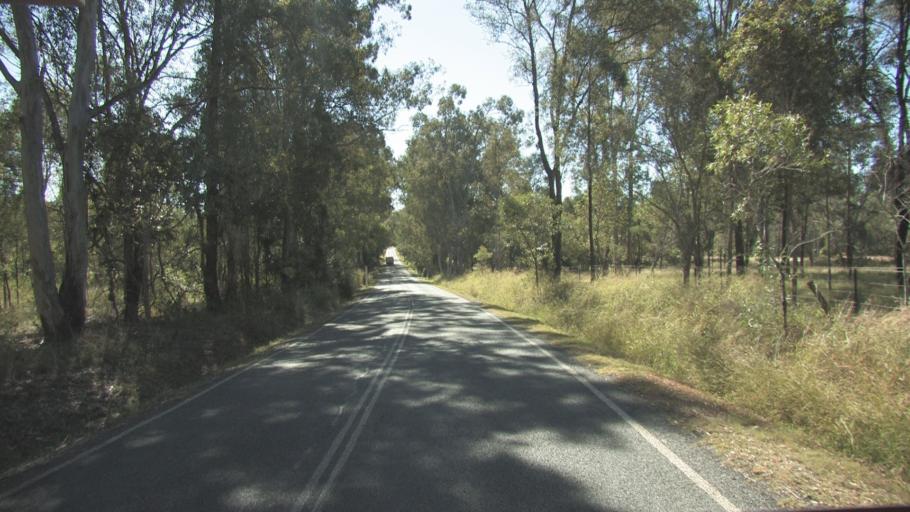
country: AU
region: Queensland
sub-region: Logan
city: Waterford West
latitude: -27.7164
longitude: 153.1418
